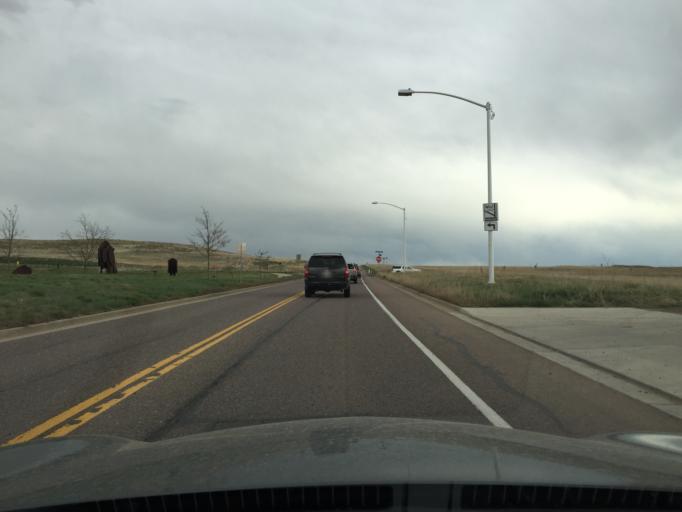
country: US
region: Colorado
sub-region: Boulder County
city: Lafayette
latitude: 39.9794
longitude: -105.0347
